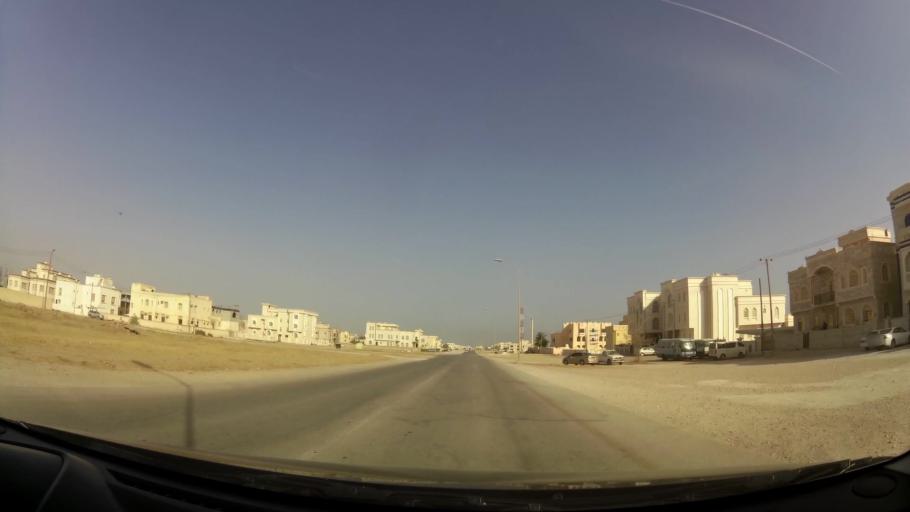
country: OM
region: Zufar
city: Salalah
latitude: 17.0207
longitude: 54.0178
